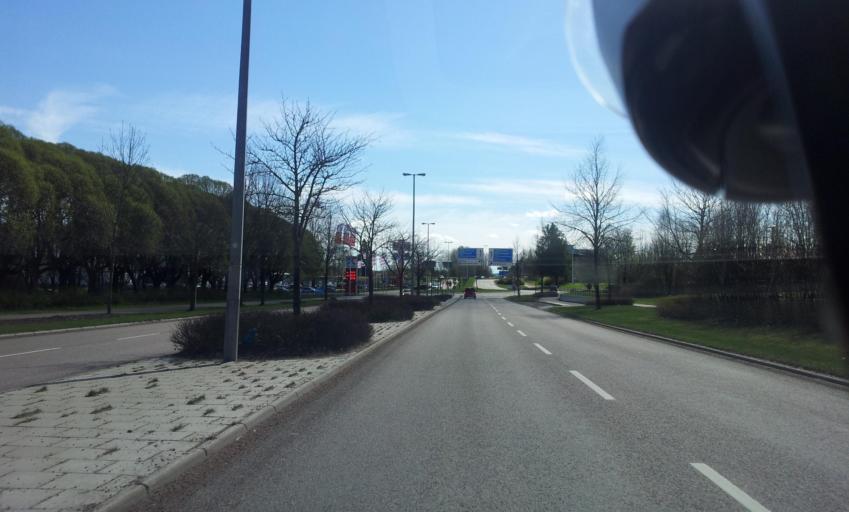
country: SE
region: Dalarna
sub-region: Borlange Kommun
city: Borlaenge
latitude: 60.4845
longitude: 15.4419
